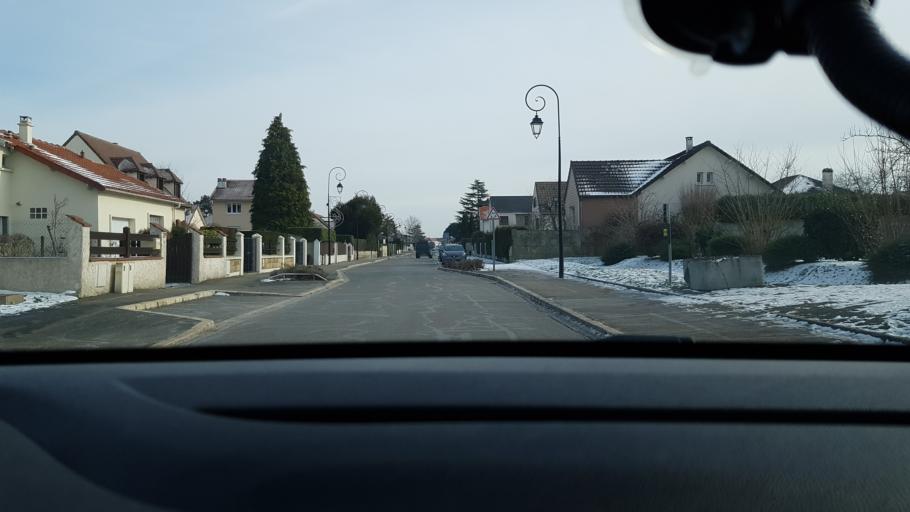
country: FR
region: Ile-de-France
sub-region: Departement des Yvelines
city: Chateaufort
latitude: 48.7226
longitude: 2.0940
